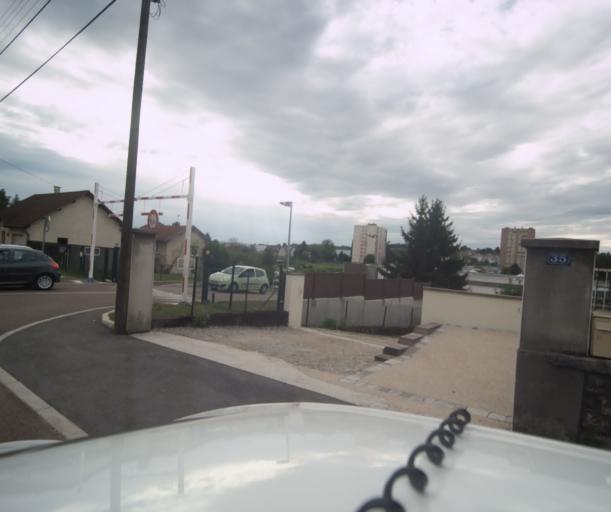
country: FR
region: Franche-Comte
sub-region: Departement du Doubs
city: Beure
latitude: 47.2313
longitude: 5.9871
